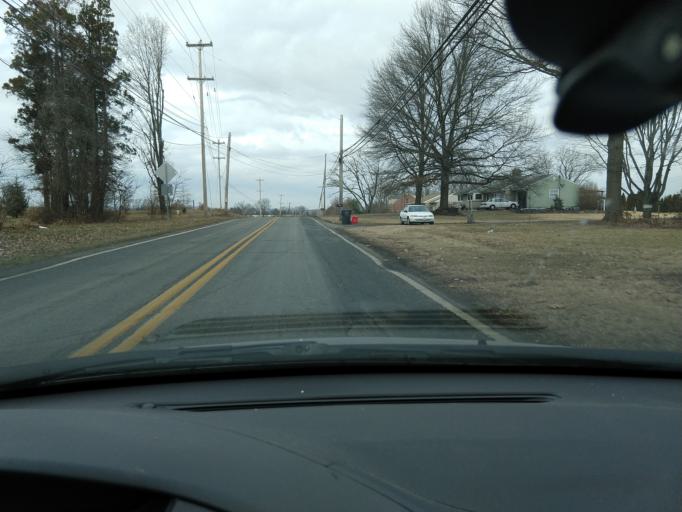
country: US
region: Pennsylvania
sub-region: Chester County
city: South Pottstown
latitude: 40.2204
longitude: -75.6571
